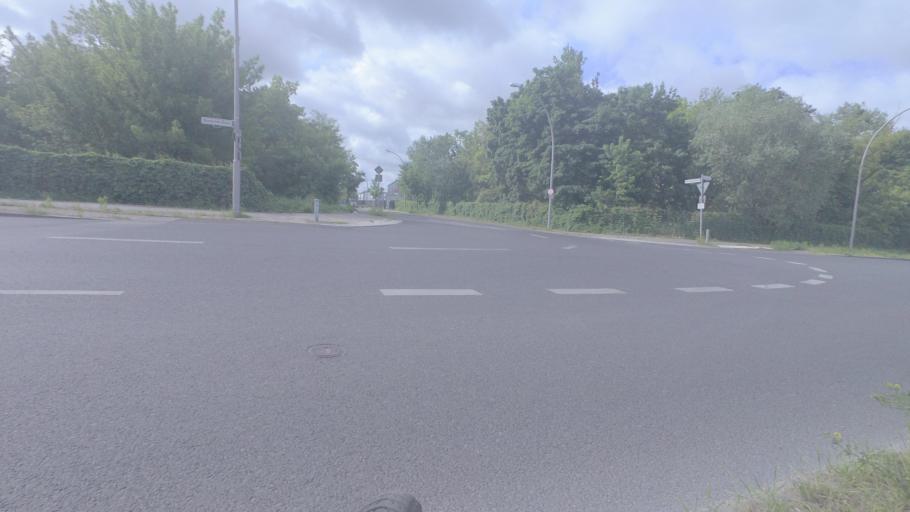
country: DE
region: Berlin
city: Staaken
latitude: 52.5358
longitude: 13.1268
